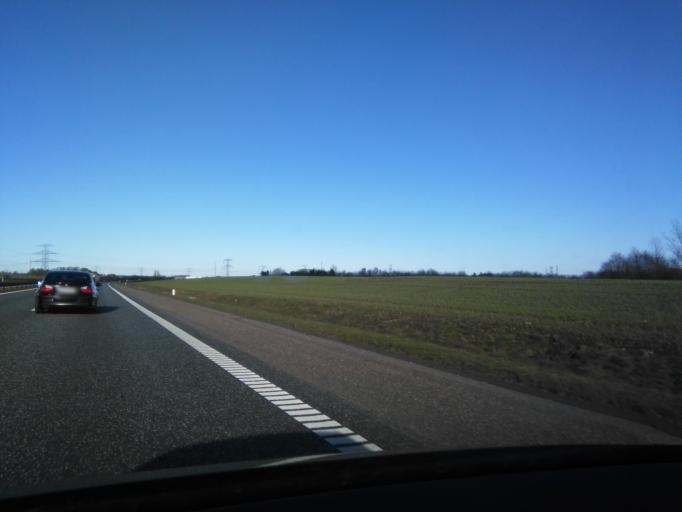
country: DK
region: Central Jutland
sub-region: Arhus Kommune
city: Trige
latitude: 56.2663
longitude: 10.1285
